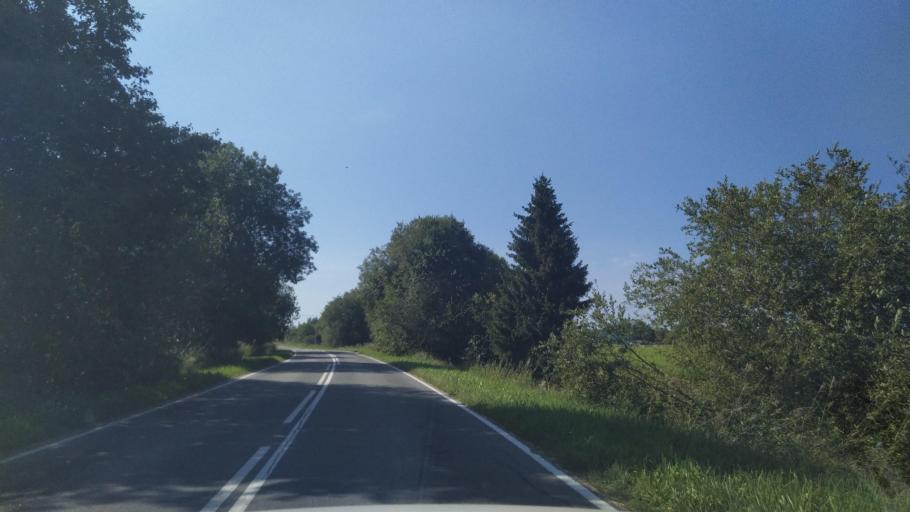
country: RU
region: Leningrad
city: Siverskiy
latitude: 59.2848
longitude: 30.0546
